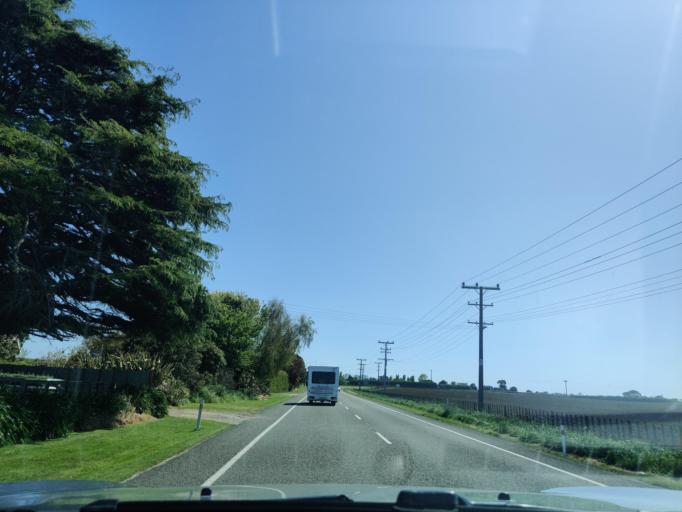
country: NZ
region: Manawatu-Wanganui
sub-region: Wanganui District
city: Wanganui
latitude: -39.8915
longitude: 175.0073
